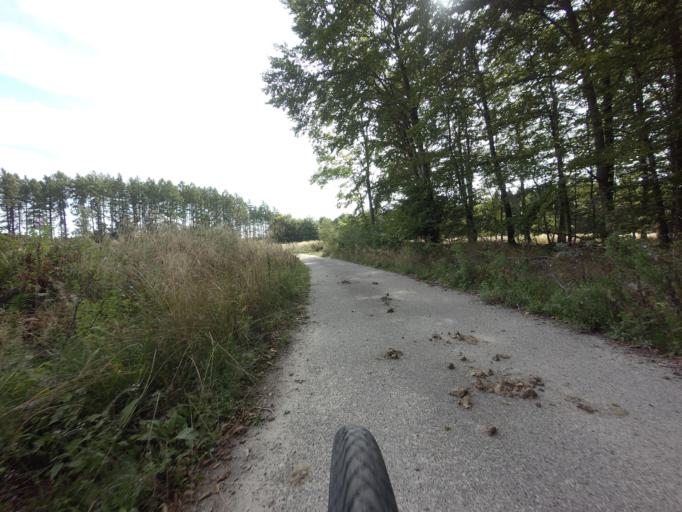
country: DK
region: Zealand
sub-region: Faxe Kommune
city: Fakse Ladeplads
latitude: 55.2340
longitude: 12.1878
